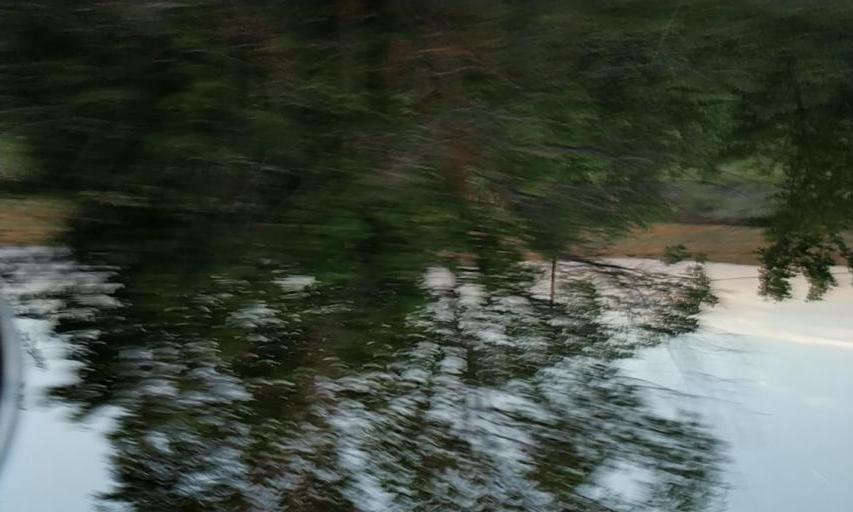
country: ES
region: Extremadura
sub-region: Provincia de Caceres
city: Alcantara
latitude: 39.7074
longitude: -6.8837
